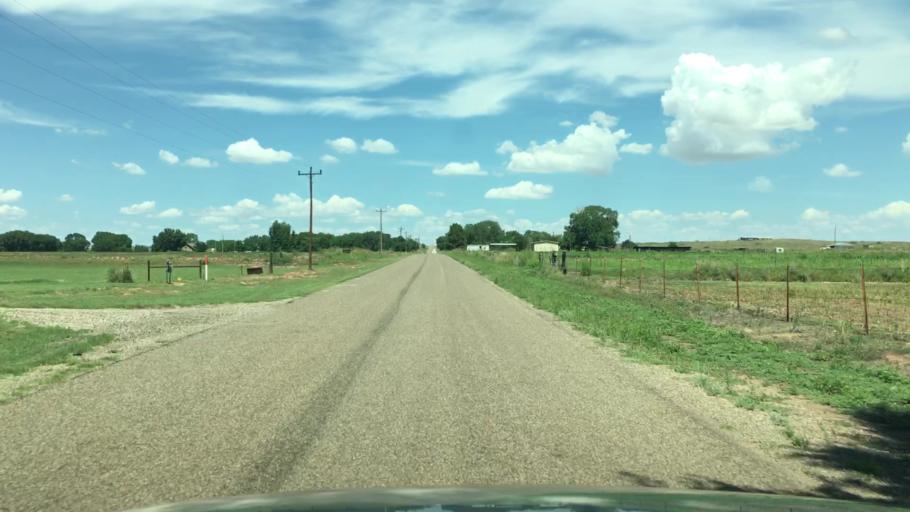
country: US
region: New Mexico
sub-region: De Baca County
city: Fort Sumner
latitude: 34.4419
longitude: -104.1936
